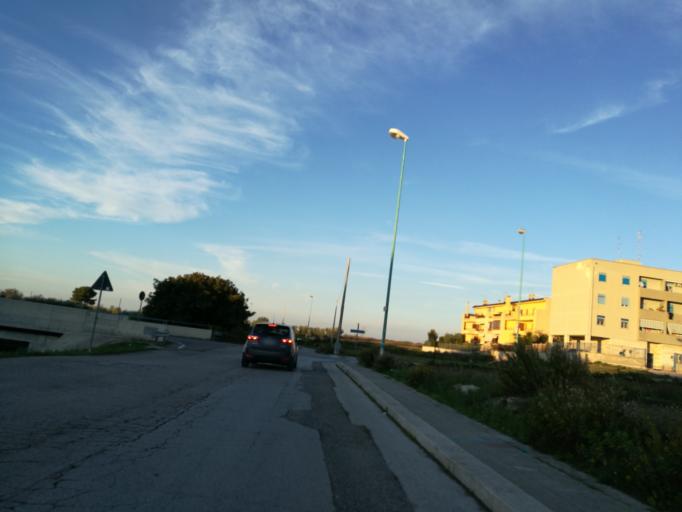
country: IT
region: Apulia
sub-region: Provincia di Bari
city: Adelfia
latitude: 41.0075
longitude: 16.8745
